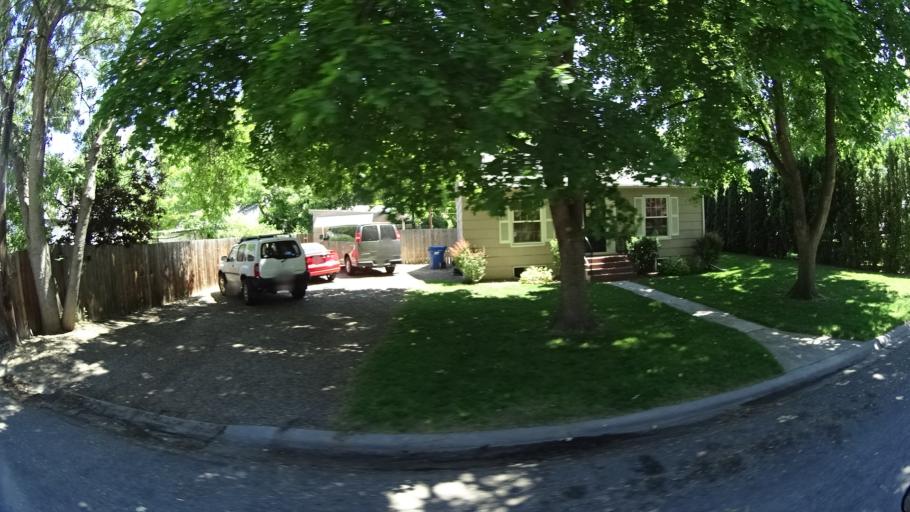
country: US
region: Idaho
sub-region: Ada County
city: Garden City
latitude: 43.6002
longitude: -116.2268
